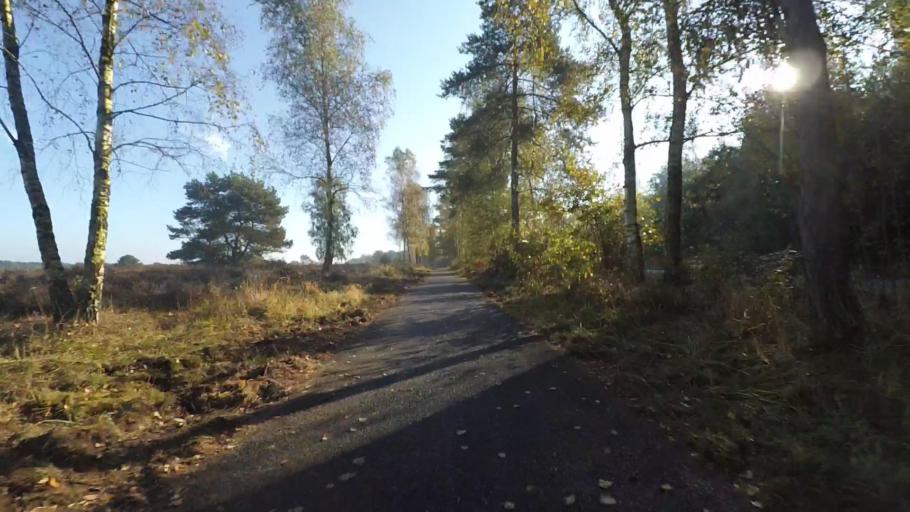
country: NL
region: Gelderland
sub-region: Gemeente Epe
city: Vaassen
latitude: 52.3165
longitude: 5.8997
